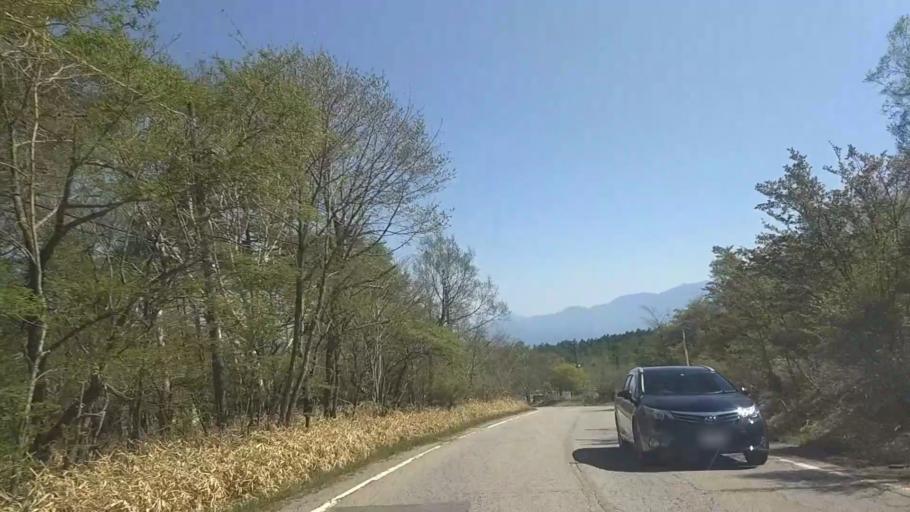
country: JP
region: Yamanashi
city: Nirasaki
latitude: 35.9390
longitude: 138.4228
